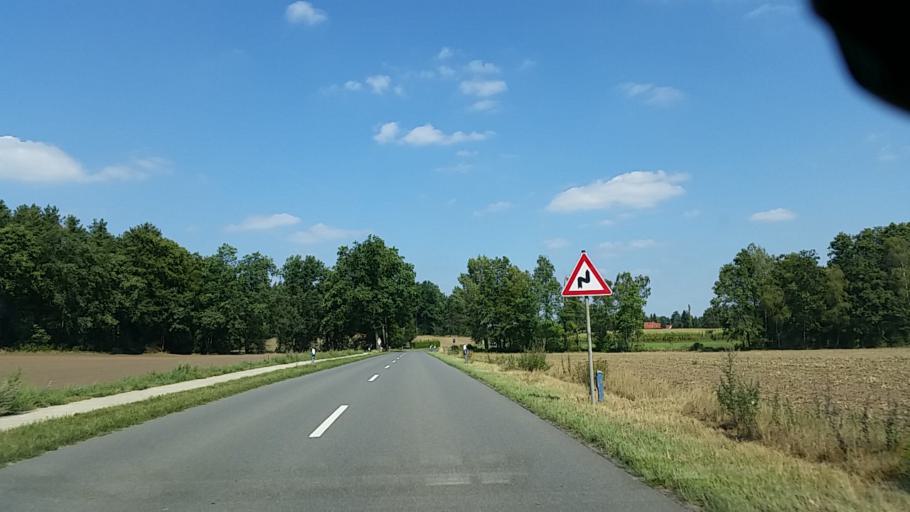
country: DE
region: Lower Saxony
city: Bienenbuttel
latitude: 53.1532
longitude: 10.4946
